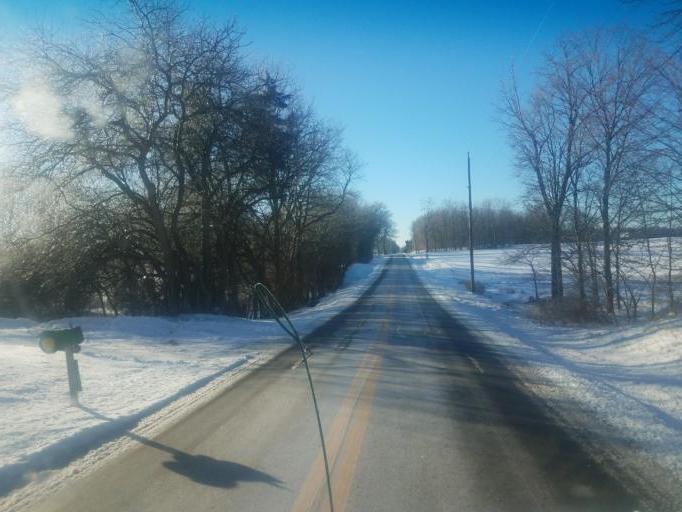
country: US
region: Ohio
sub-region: Delaware County
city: Sunbury
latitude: 40.2299
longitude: -82.9119
